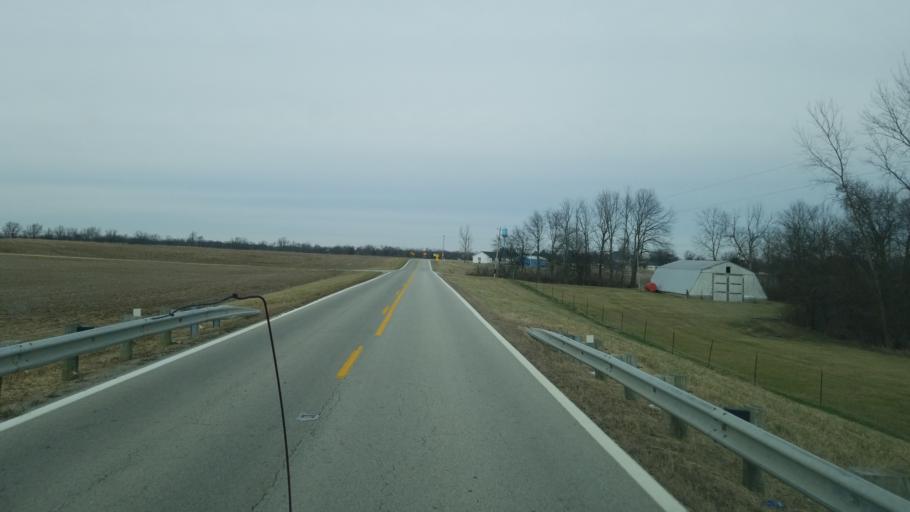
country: US
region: Ohio
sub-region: Pickaway County
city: Williamsport
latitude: 39.5008
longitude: -83.1640
